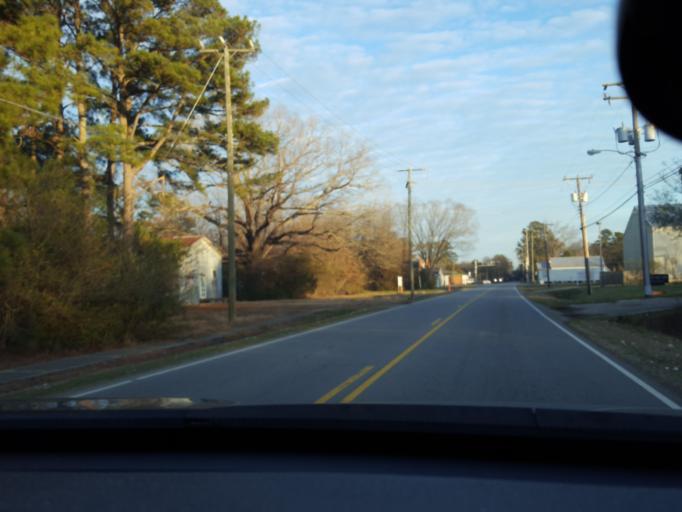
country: US
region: North Carolina
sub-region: Northampton County
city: Jackson
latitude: 36.2727
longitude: -77.2779
